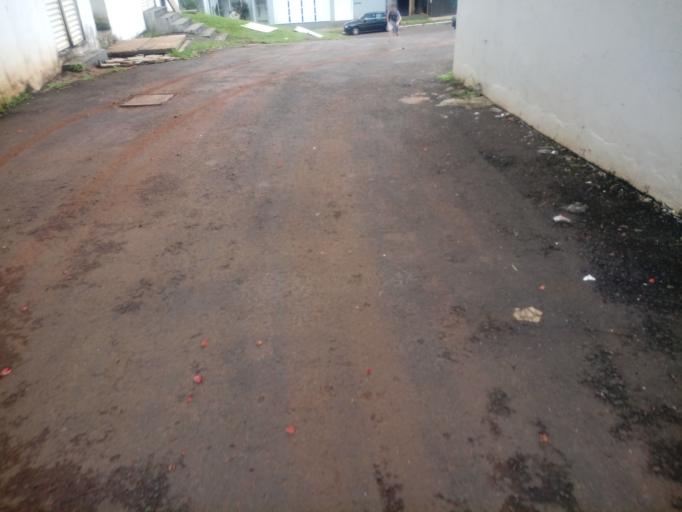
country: BR
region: Santa Catarina
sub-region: Chapeco
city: Chapeco
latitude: -27.1034
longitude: -52.6064
